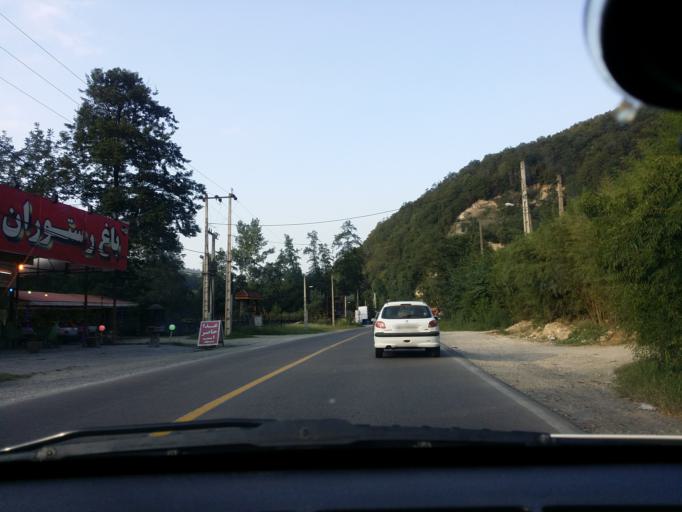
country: IR
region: Mazandaran
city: Chalus
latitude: 36.6043
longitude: 51.3851
